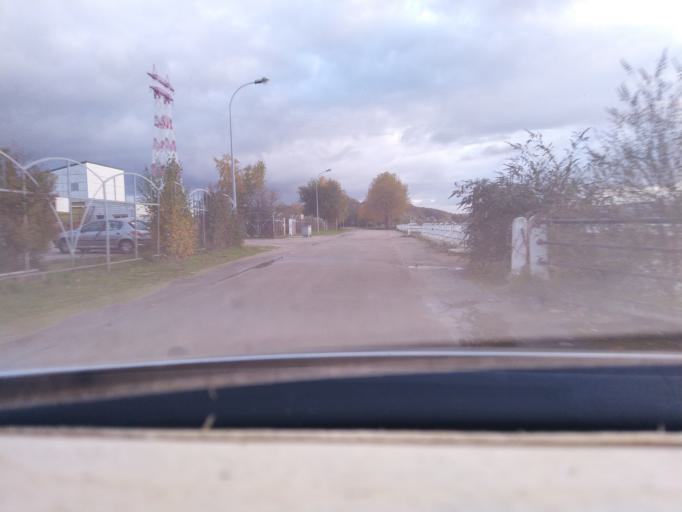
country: FR
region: Haute-Normandie
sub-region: Departement de la Seine-Maritime
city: Le Trait
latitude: 49.4611
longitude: 0.8182
